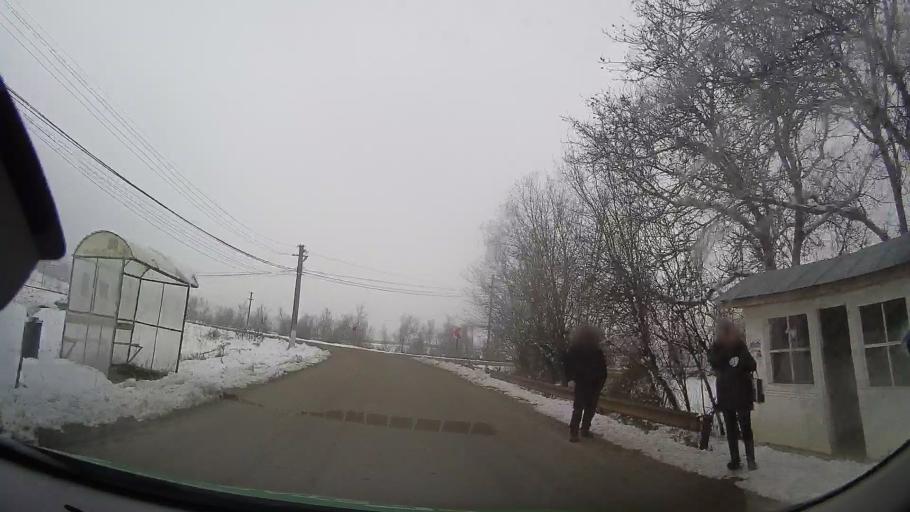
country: RO
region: Bacau
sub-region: Comuna Vultureni
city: Vultureni
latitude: 46.3985
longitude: 27.2732
